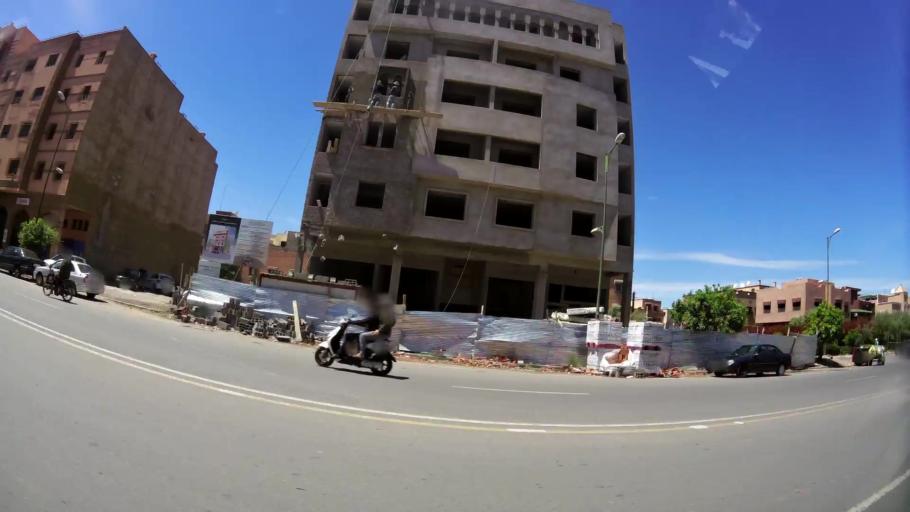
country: MA
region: Marrakech-Tensift-Al Haouz
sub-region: Marrakech
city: Marrakesh
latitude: 31.6370
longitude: -8.0581
